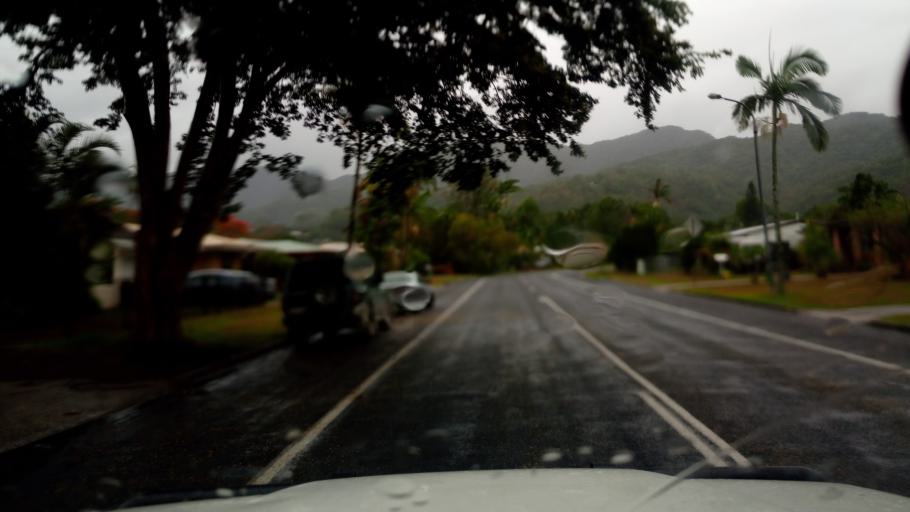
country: AU
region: Queensland
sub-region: Cairns
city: Woree
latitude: -16.9409
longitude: 145.7336
